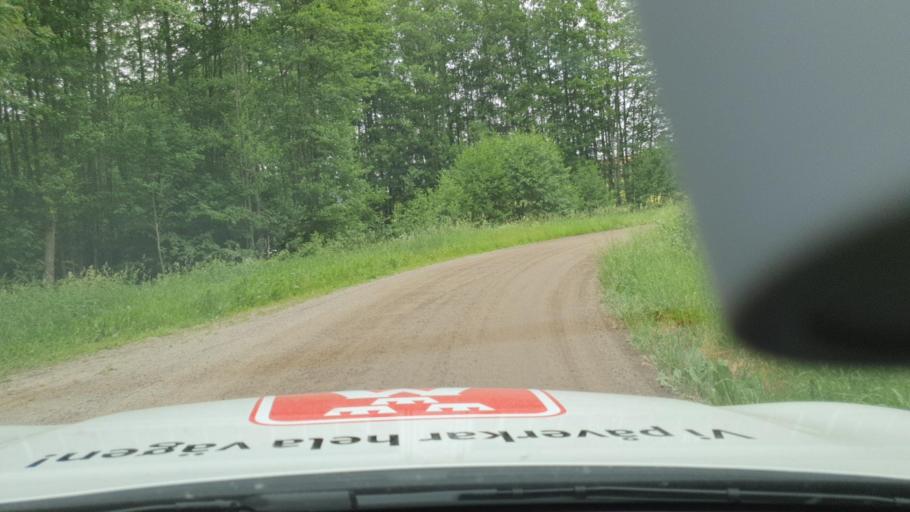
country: SE
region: Vaestra Goetaland
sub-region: Hjo Kommun
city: Hjo
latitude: 58.2028
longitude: 14.1747
